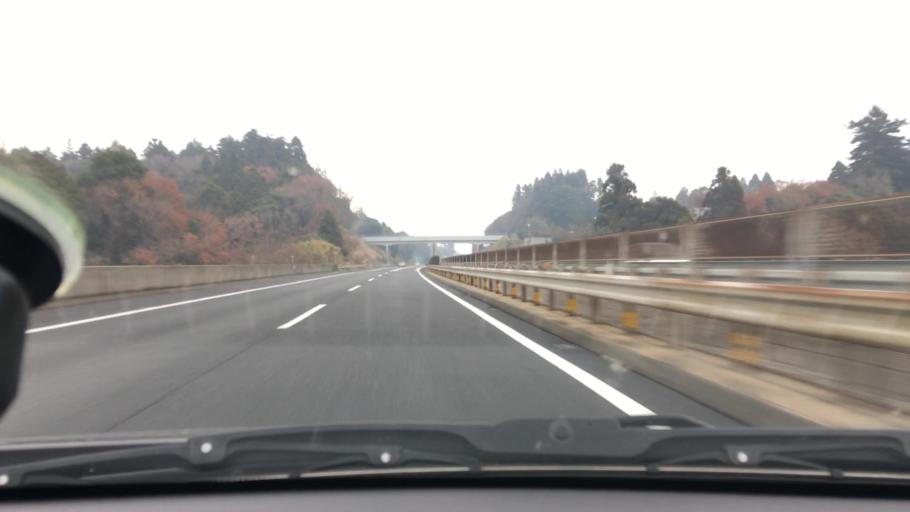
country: JP
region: Chiba
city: Narita
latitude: 35.7941
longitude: 140.3523
